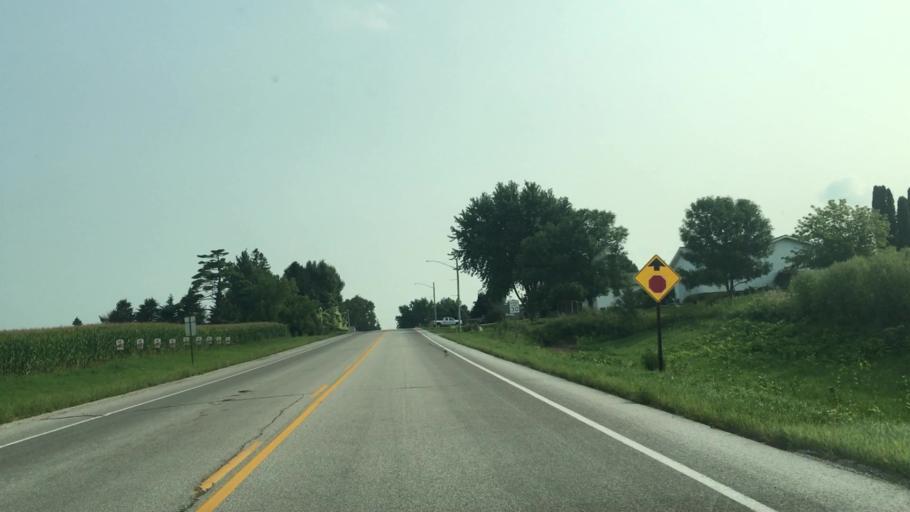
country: US
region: Minnesota
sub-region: Fillmore County
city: Harmony
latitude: 43.5355
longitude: -91.9297
